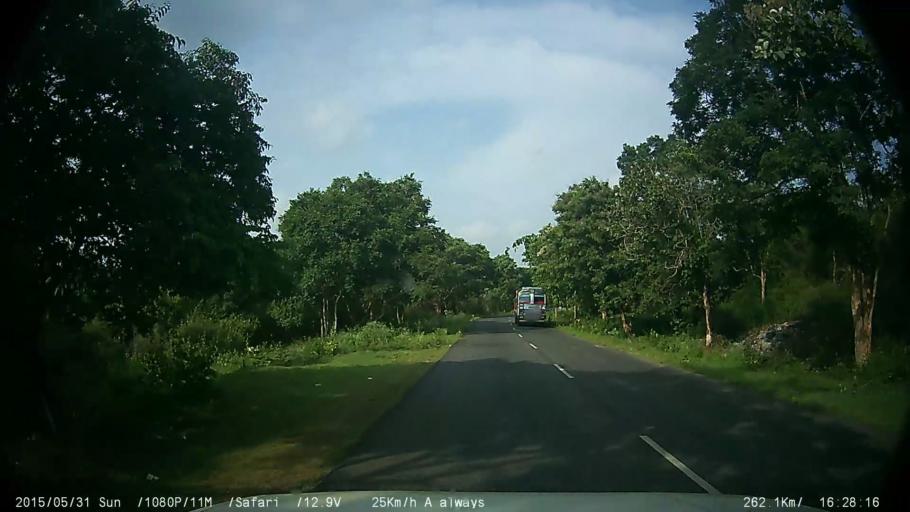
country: IN
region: Karnataka
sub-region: Chamrajnagar
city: Gundlupet
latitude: 11.7685
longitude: 76.5401
